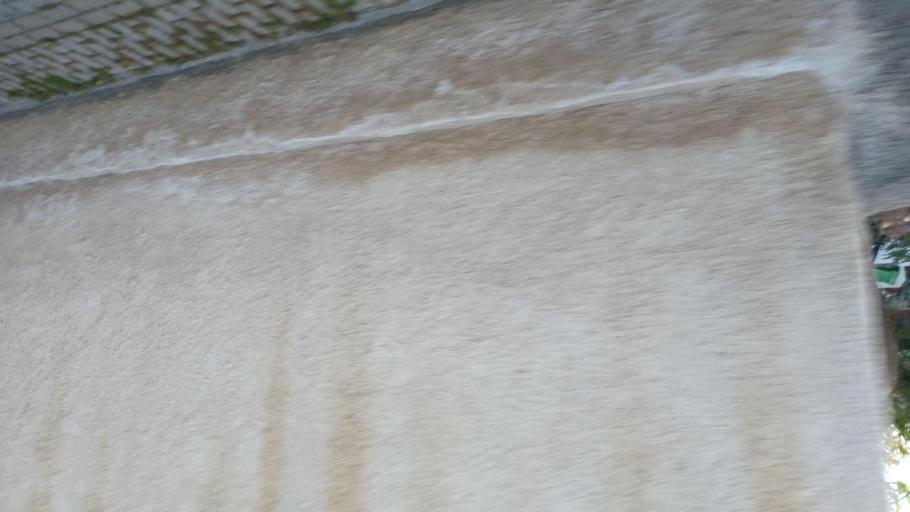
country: CY
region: Lefkosia
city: Akaki
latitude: 35.1669
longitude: 33.1470
